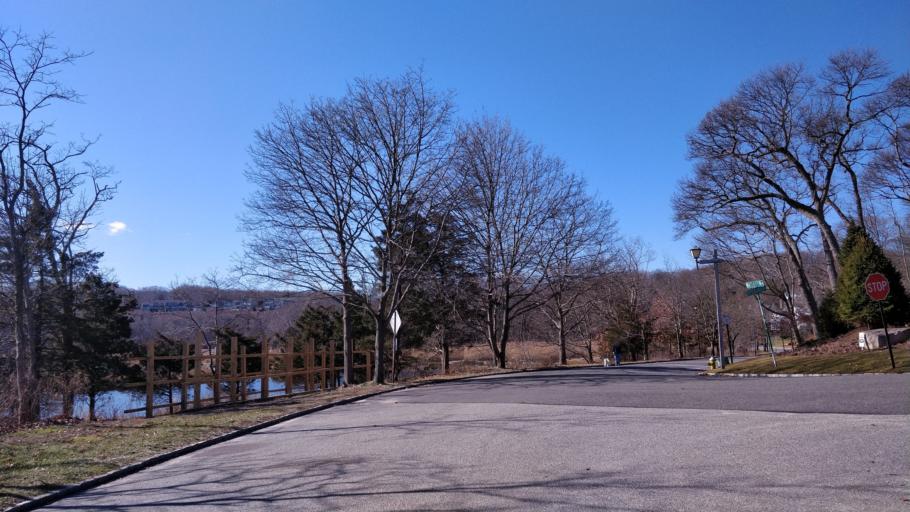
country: US
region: New York
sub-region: Suffolk County
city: Mount Sinai
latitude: 40.9576
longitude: -73.0417
